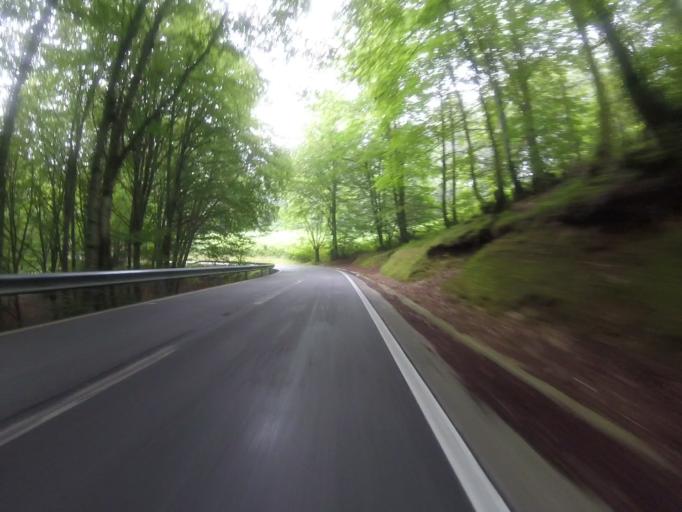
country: ES
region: Navarre
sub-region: Provincia de Navarra
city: Ezkurra
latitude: 43.0831
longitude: -1.8617
